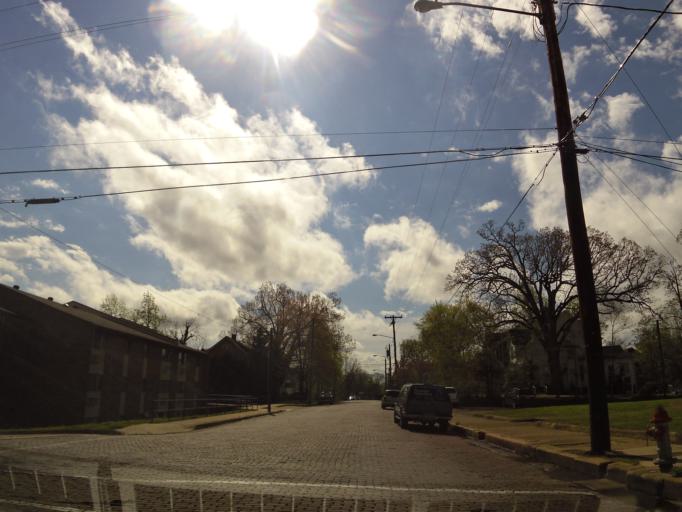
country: US
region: Missouri
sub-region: Butler County
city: Poplar Bluff
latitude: 36.7609
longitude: -90.3947
